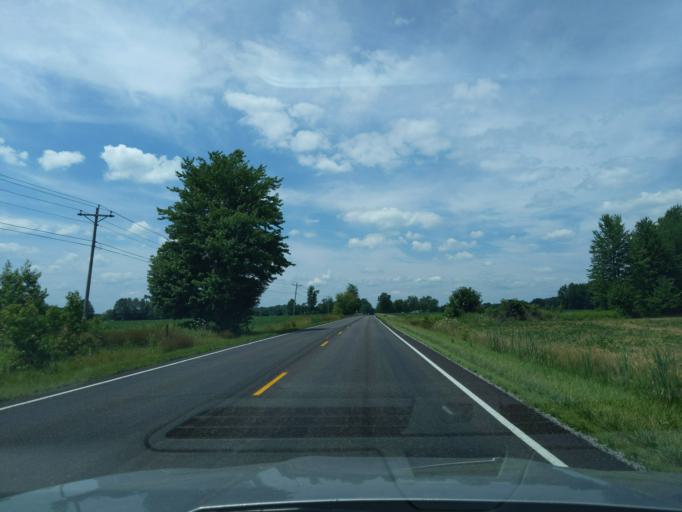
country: US
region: Indiana
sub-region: Decatur County
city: Greensburg
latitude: 39.2736
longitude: -85.3945
